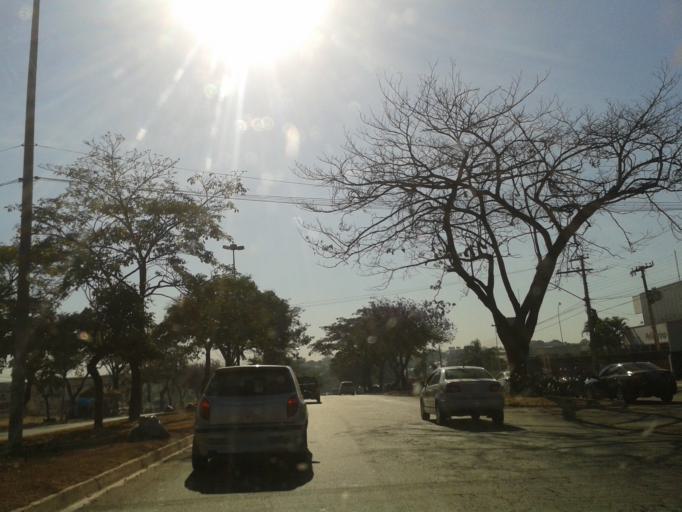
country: BR
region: Goias
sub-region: Goiania
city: Goiania
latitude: -16.6943
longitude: -49.3235
